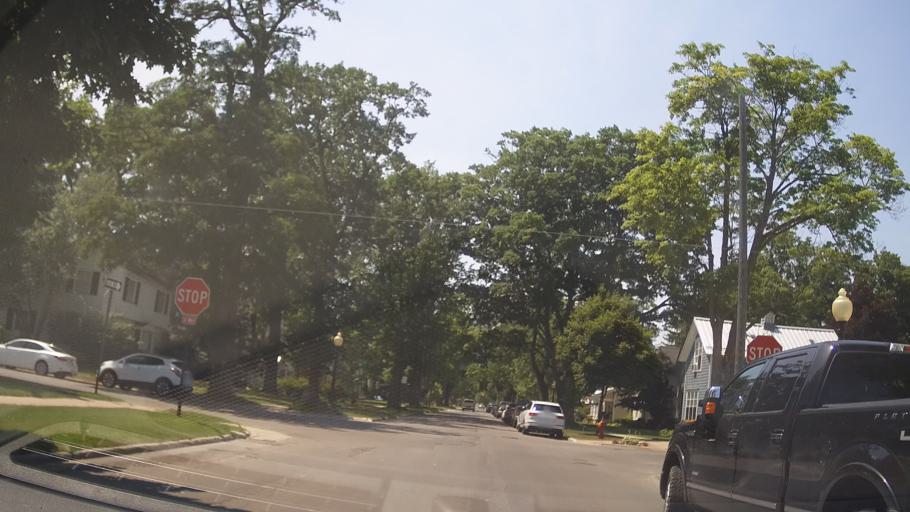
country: US
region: Michigan
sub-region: Grand Traverse County
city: Traverse City
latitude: 44.7605
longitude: -85.6302
